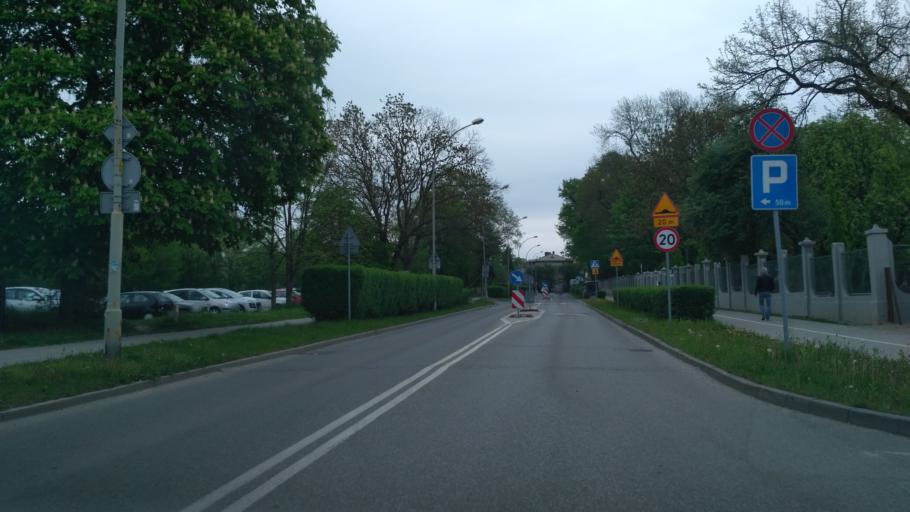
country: PL
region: Lesser Poland Voivodeship
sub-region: Powiat tarnowski
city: Tarnow
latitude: 50.0217
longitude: 20.9843
